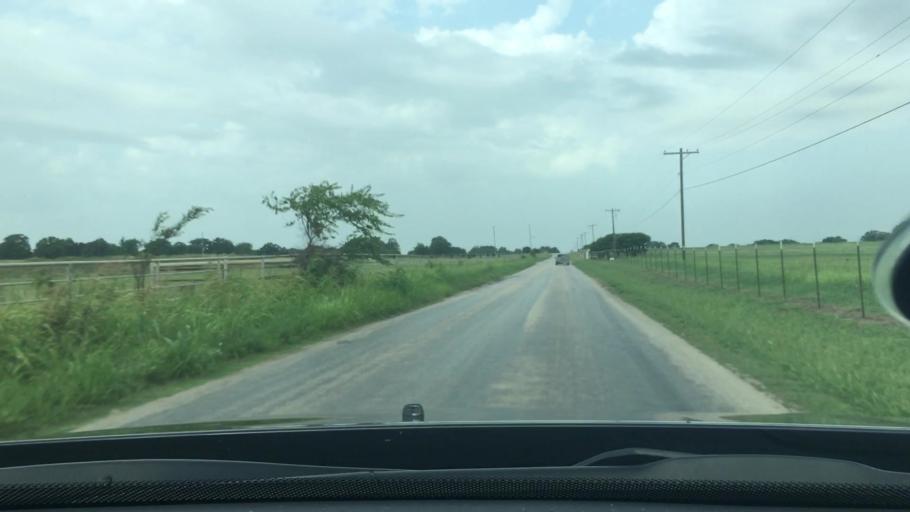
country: US
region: Oklahoma
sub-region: Carter County
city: Lone Grove
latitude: 34.2020
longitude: -97.2542
